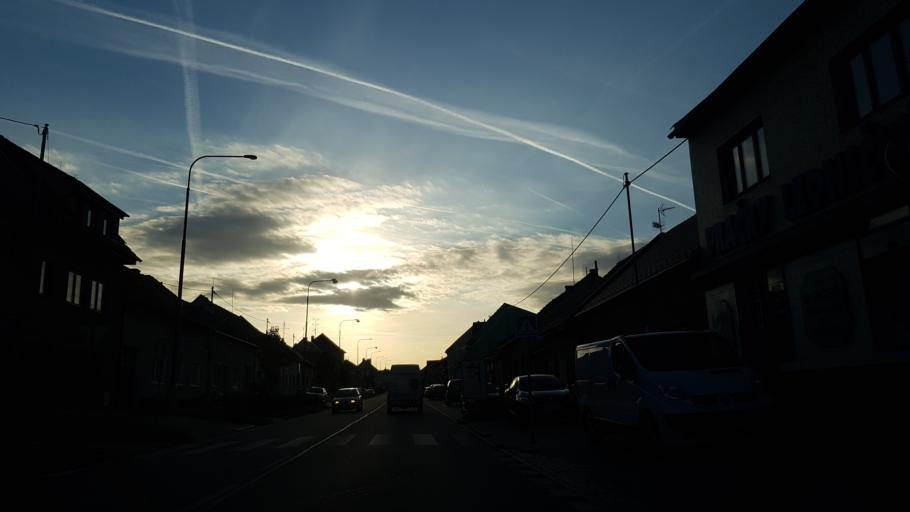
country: CZ
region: Zlin
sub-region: Okres Uherske Hradiste
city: Stare Mesto
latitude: 49.0754
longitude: 17.4387
